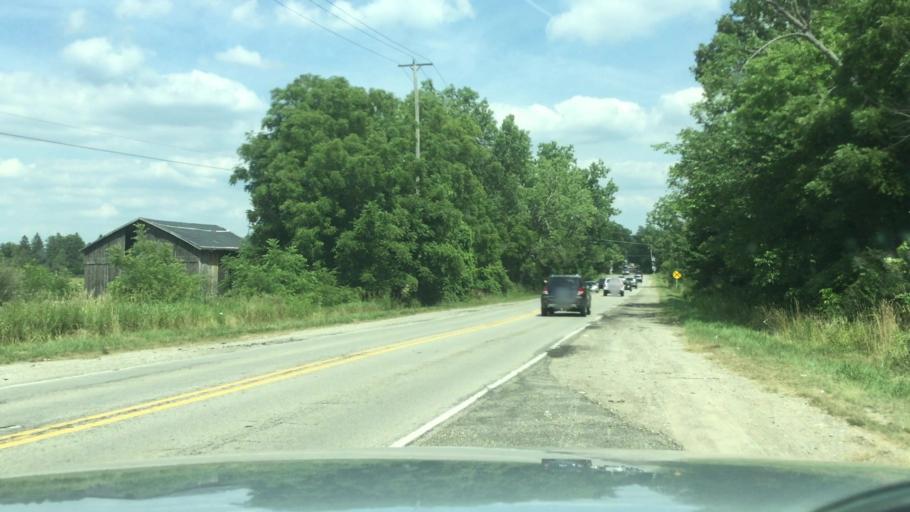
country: US
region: Michigan
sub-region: Genesee County
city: Grand Blanc
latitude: 42.9446
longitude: -83.6454
